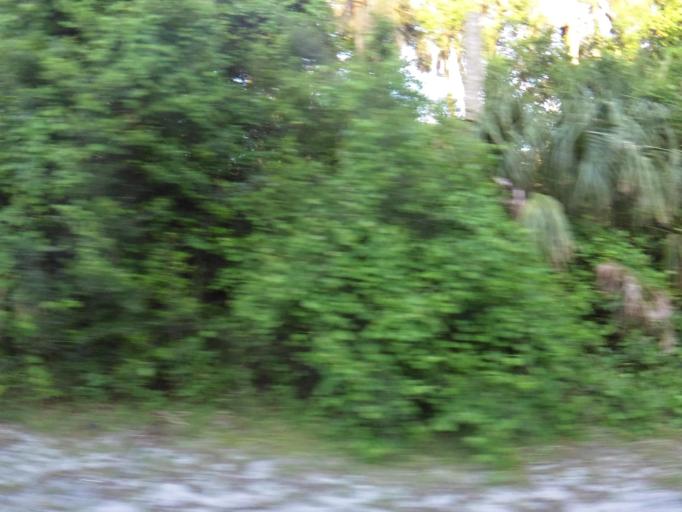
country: US
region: Florida
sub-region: Duval County
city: Atlantic Beach
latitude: 30.3734
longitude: -81.3996
